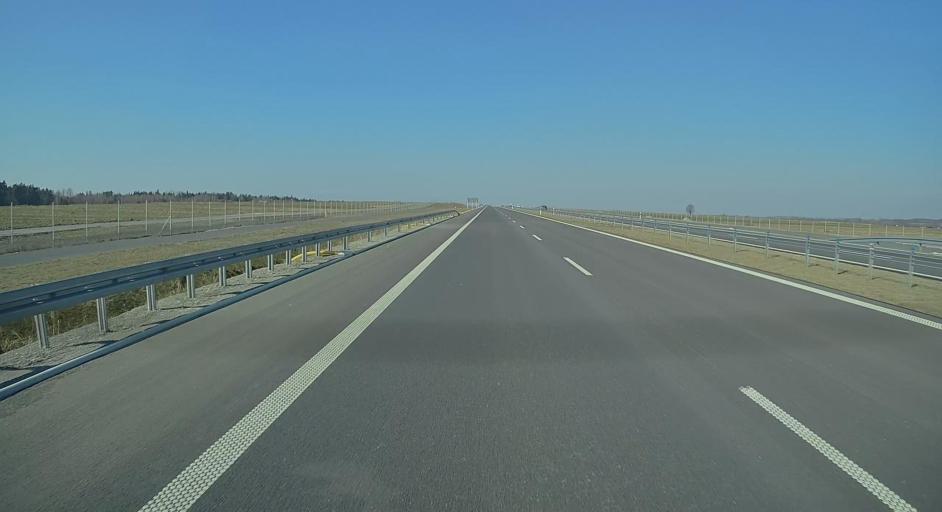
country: PL
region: Lublin Voivodeship
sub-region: Powiat janowski
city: Modliborzyce
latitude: 50.7418
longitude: 22.3133
